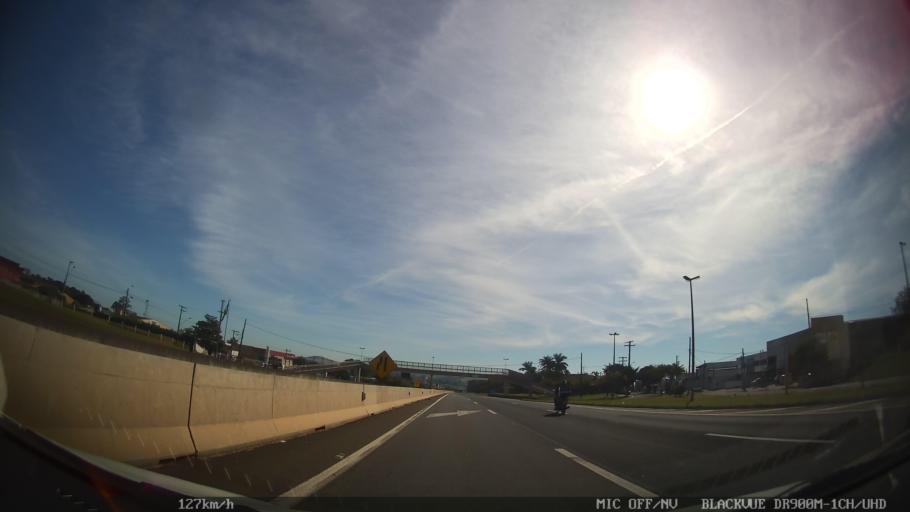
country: BR
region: Sao Paulo
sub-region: Araras
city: Araras
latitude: -22.3753
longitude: -47.3944
